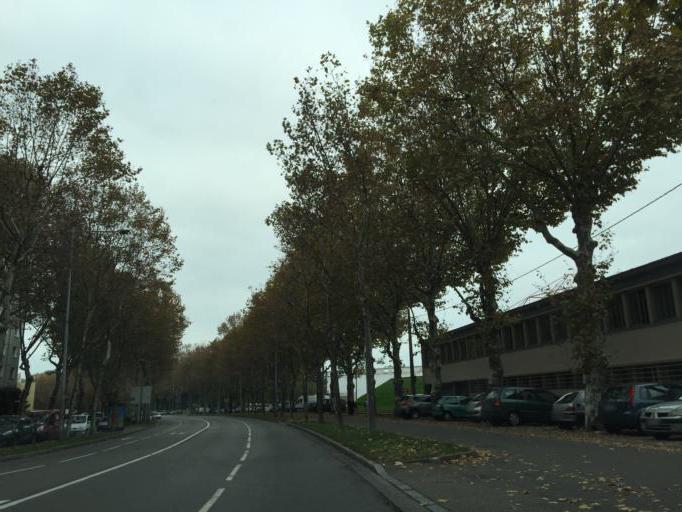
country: FR
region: Rhone-Alpes
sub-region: Departement de la Loire
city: Saint-Etienne
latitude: 45.4473
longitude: 4.3967
